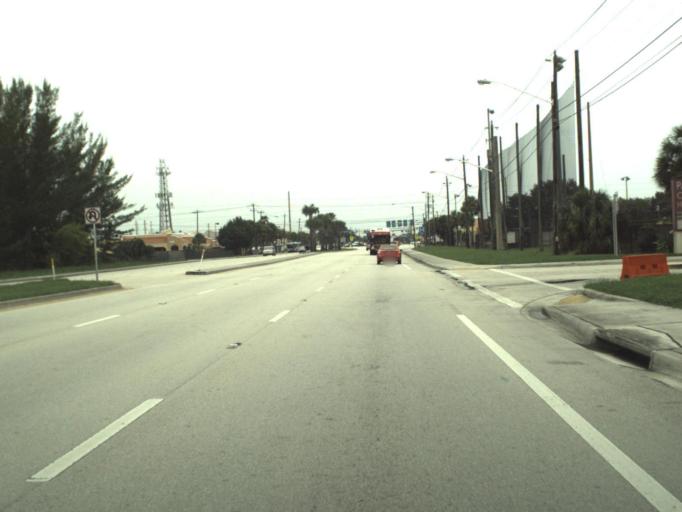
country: US
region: Florida
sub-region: Palm Beach County
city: Mangonia Park
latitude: 26.7559
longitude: -80.1087
